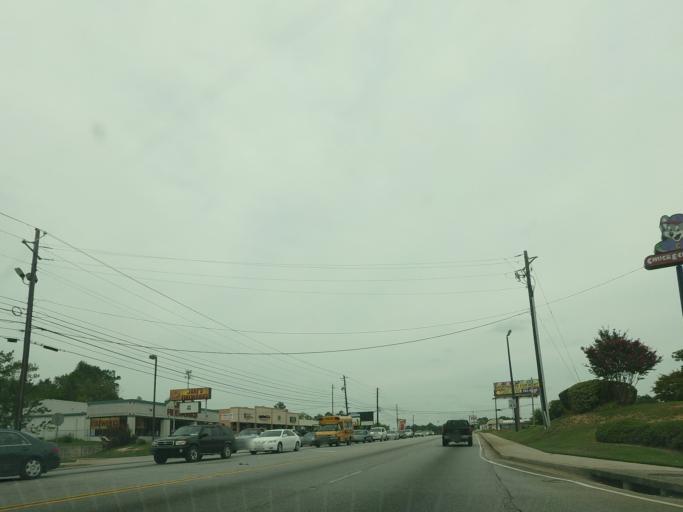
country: US
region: Georgia
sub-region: Bibb County
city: Macon
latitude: 32.8208
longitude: -83.6890
